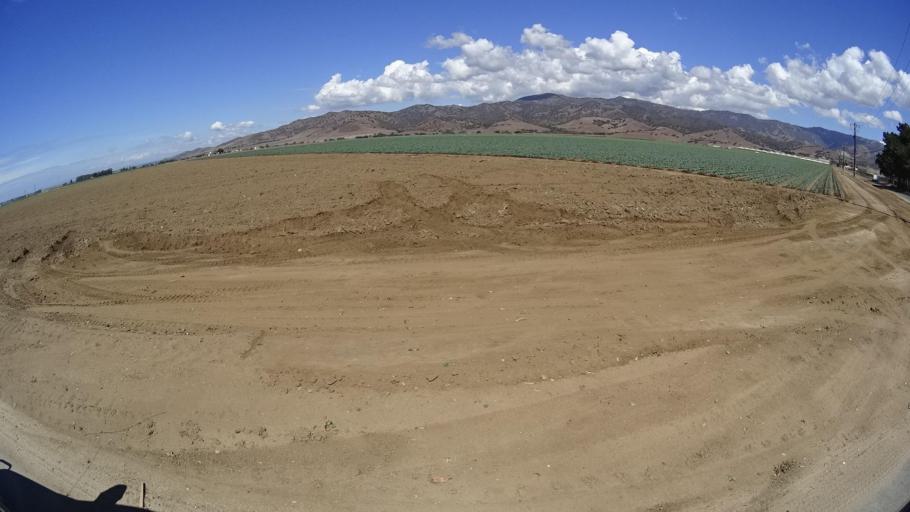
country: US
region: California
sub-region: Monterey County
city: Chualar
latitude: 36.6192
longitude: -121.5103
